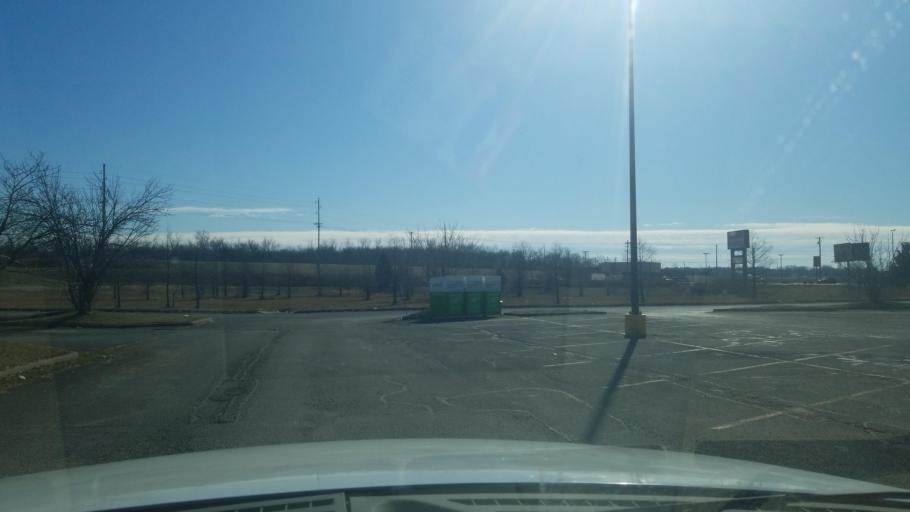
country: US
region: Illinois
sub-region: Saline County
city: Harrisburg
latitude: 37.7470
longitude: -88.5239
